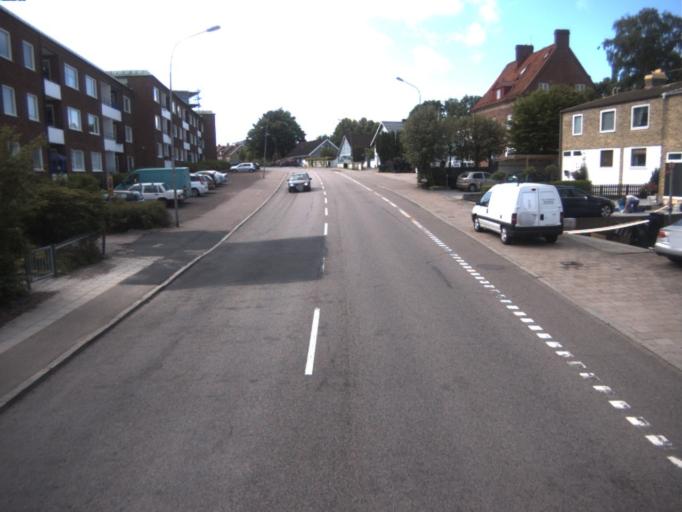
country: SE
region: Skane
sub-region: Helsingborg
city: Helsingborg
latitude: 56.0646
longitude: 12.6987
